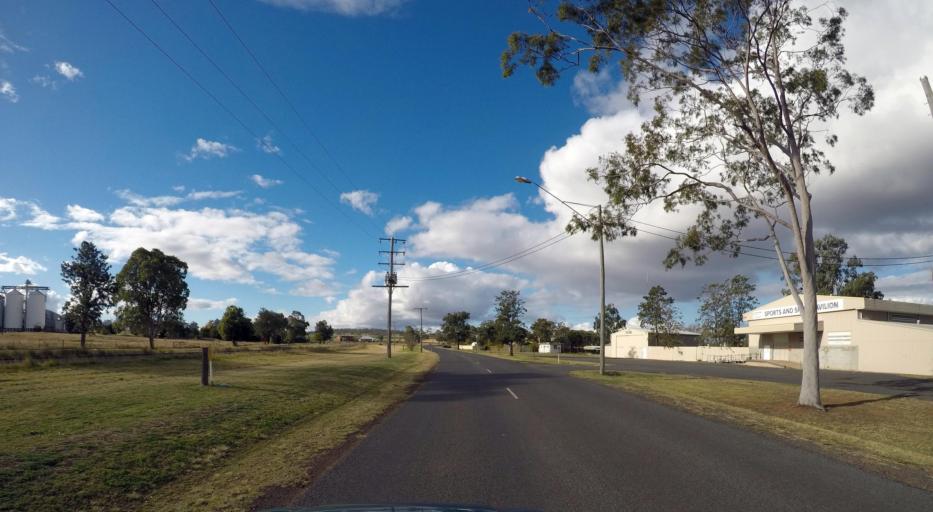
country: AU
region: Queensland
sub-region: Toowoomba
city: Westbrook
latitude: -27.7117
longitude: 151.6412
